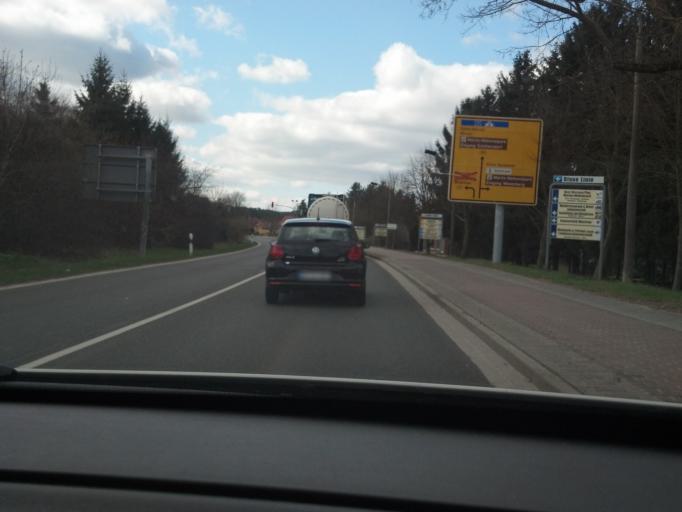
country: DE
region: Mecklenburg-Vorpommern
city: Wesenberg
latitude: 53.2803
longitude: 12.9656
